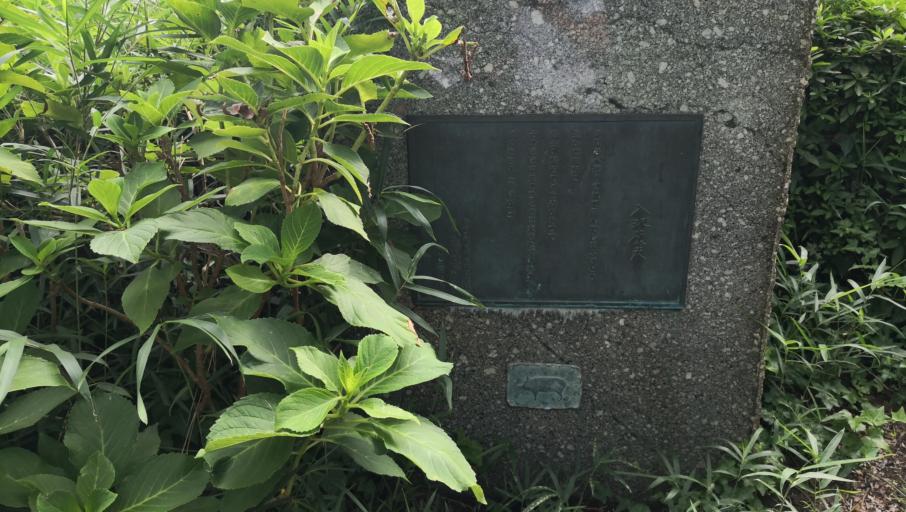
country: JP
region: Gunma
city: Maebashi-shi
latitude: 36.3950
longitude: 139.0711
